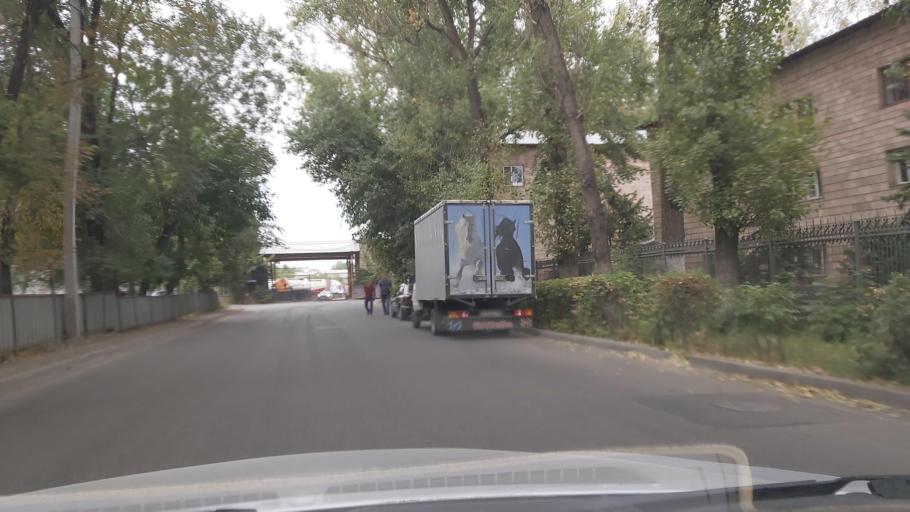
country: KZ
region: Almaty Oblysy
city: Pervomayskiy
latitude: 43.3541
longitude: 76.9804
